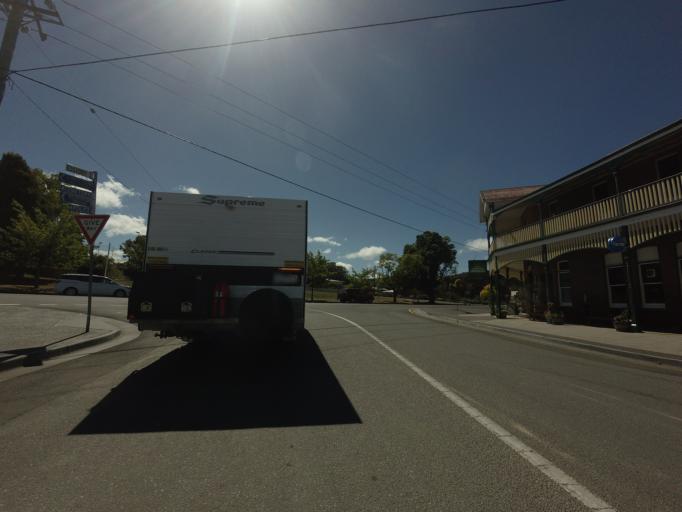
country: AU
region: Tasmania
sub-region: Break O'Day
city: St Helens
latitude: -41.5798
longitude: 148.1859
